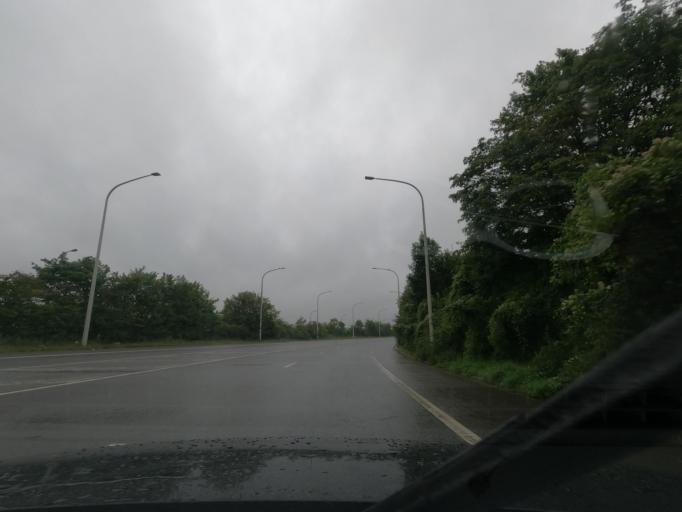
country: BE
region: Wallonia
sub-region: Province de Liege
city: Flemalle-Haute
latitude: 50.6072
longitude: 5.4376
